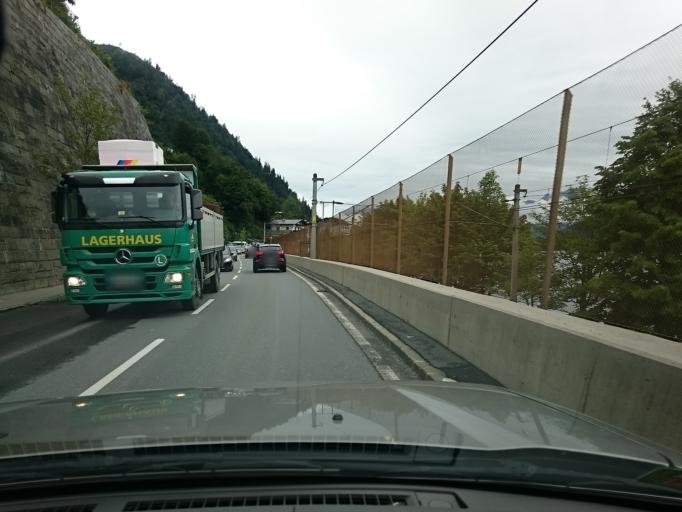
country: AT
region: Salzburg
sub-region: Politischer Bezirk Zell am See
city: Zell am See
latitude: 47.3313
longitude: 12.7970
